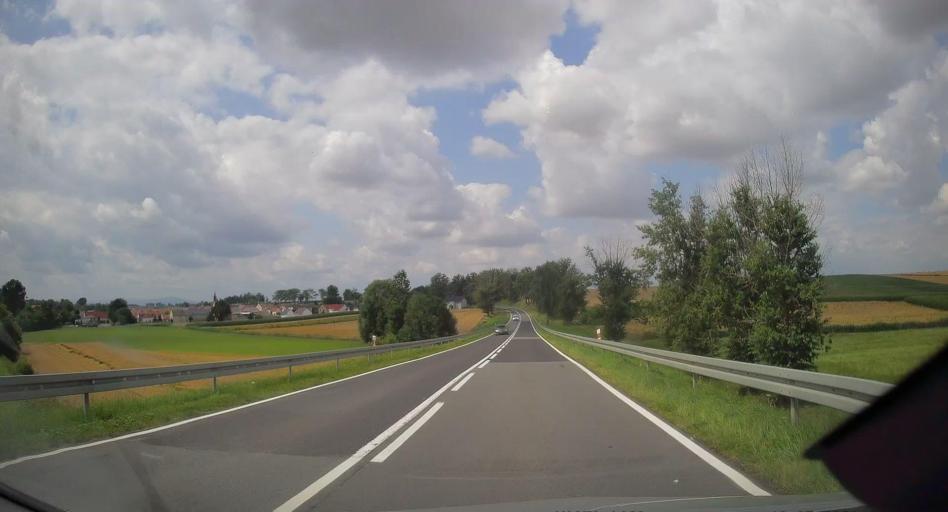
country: PL
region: Opole Voivodeship
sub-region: Powiat prudnicki
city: Raclawice Slaskie
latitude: 50.3459
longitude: 17.7485
